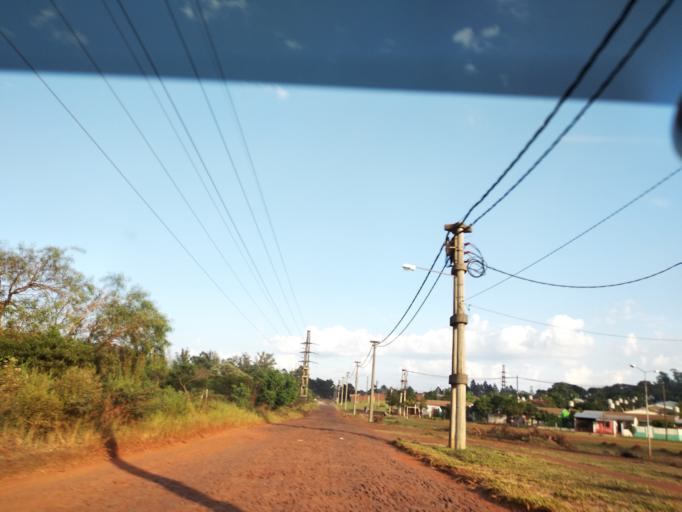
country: AR
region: Misiones
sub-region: Departamento de Capital
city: Posadas
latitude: -27.4417
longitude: -55.9461
